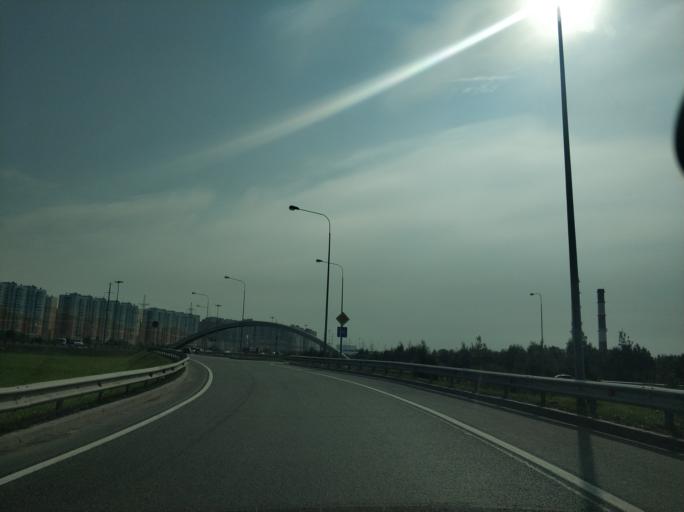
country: RU
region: Leningrad
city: Murino
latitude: 60.0342
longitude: 30.4395
